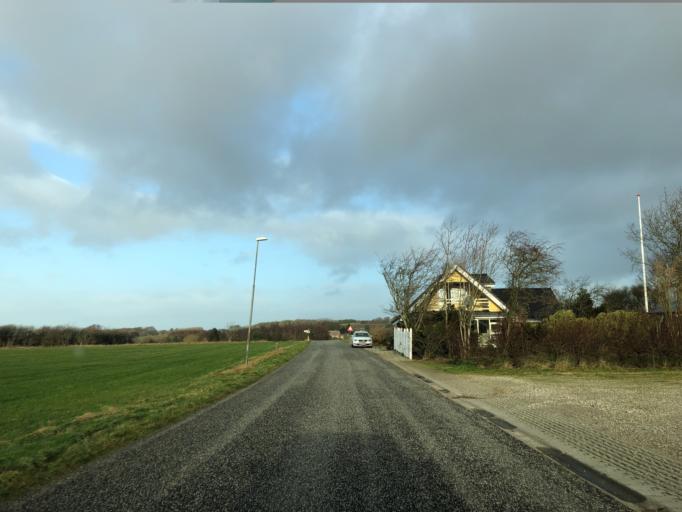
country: DK
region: Central Jutland
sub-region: Ringkobing-Skjern Kommune
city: Videbaek
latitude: 56.1785
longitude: 8.5386
